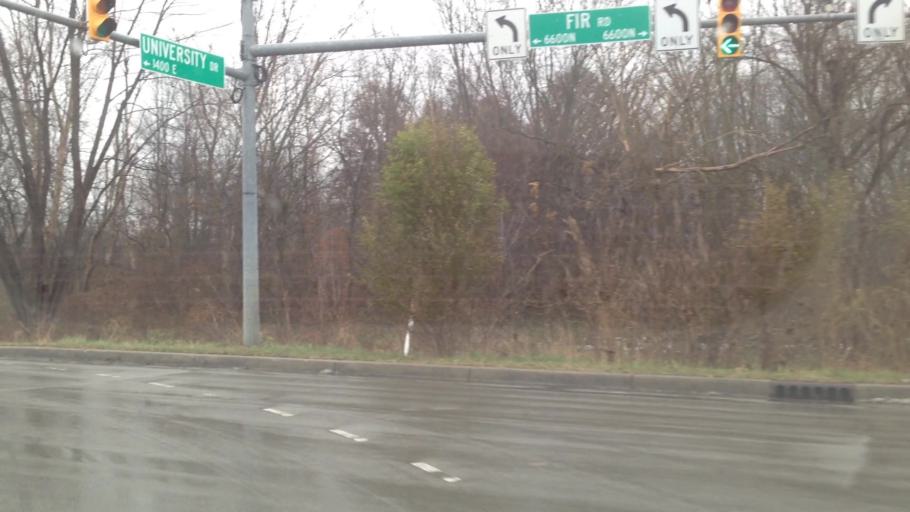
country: US
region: Indiana
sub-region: Saint Joseph County
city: Mishawaka
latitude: 41.7217
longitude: -86.1634
